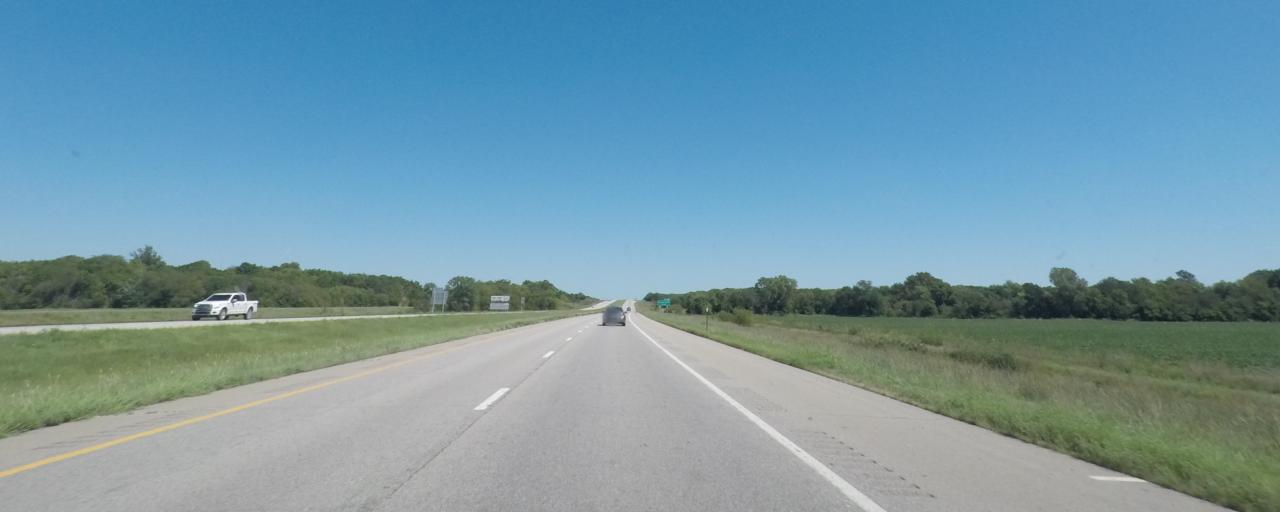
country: US
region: Kansas
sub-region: Lyon County
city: Emporia
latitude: 38.4112
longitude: -96.1106
